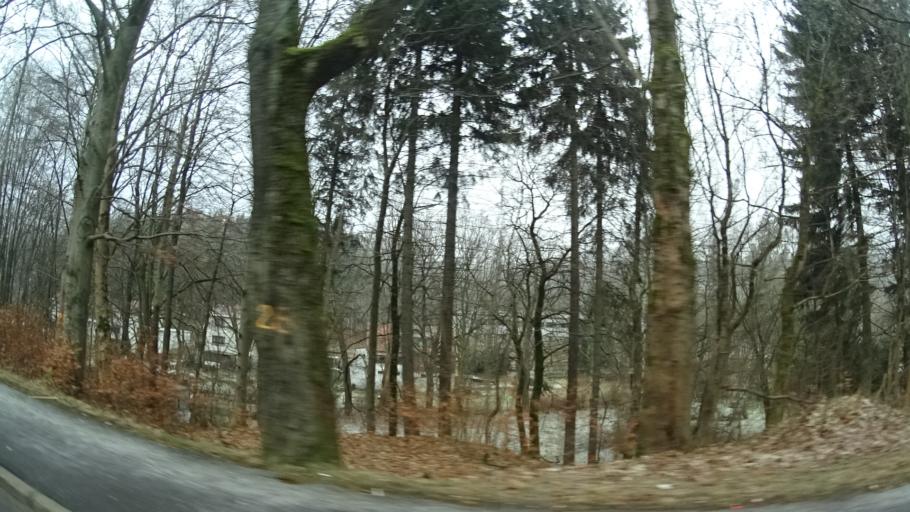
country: DE
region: Thuringia
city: Zella-Mehlis
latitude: 50.6644
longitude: 10.6838
